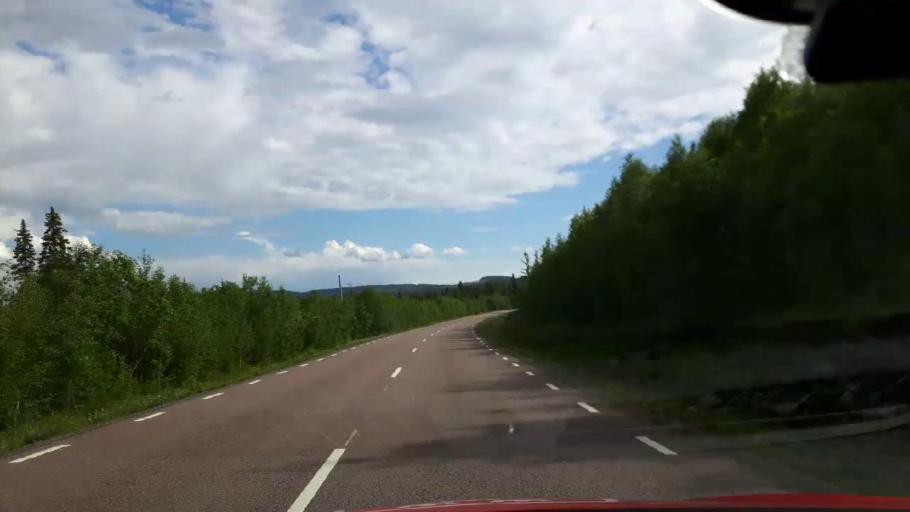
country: SE
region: Jaemtland
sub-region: Krokoms Kommun
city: Valla
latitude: 63.9246
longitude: 14.2139
